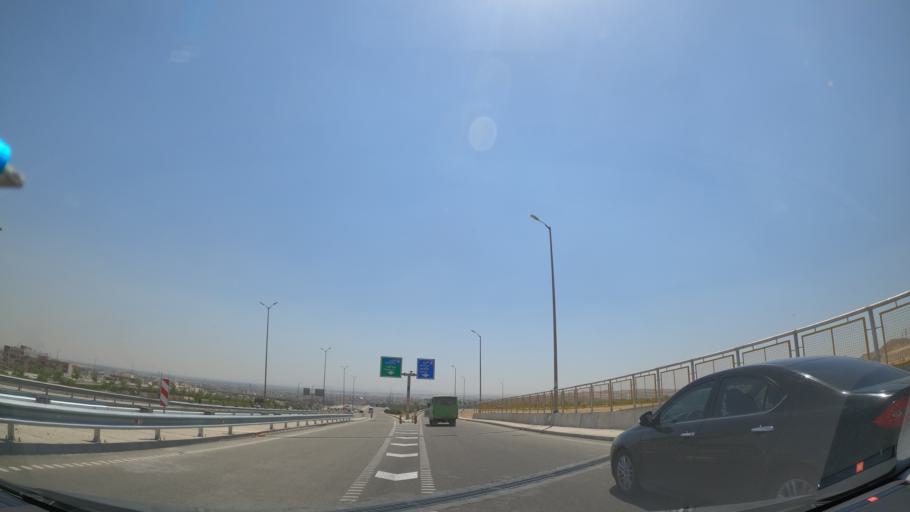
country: IR
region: Tehran
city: Shahr-e Qods
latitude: 35.7458
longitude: 51.1274
